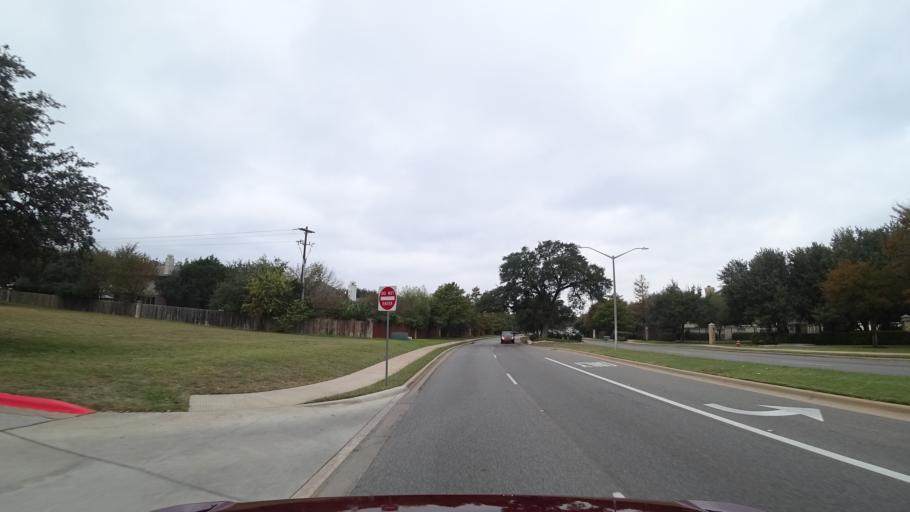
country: US
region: Texas
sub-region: Williamson County
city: Cedar Park
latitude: 30.4825
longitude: -97.8352
